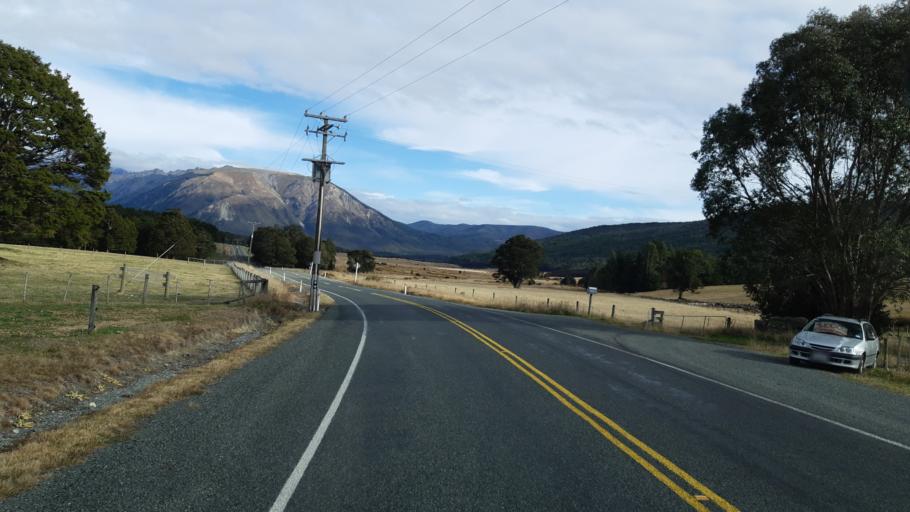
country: NZ
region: Tasman
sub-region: Tasman District
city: Wakefield
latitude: -41.7880
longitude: 172.8860
